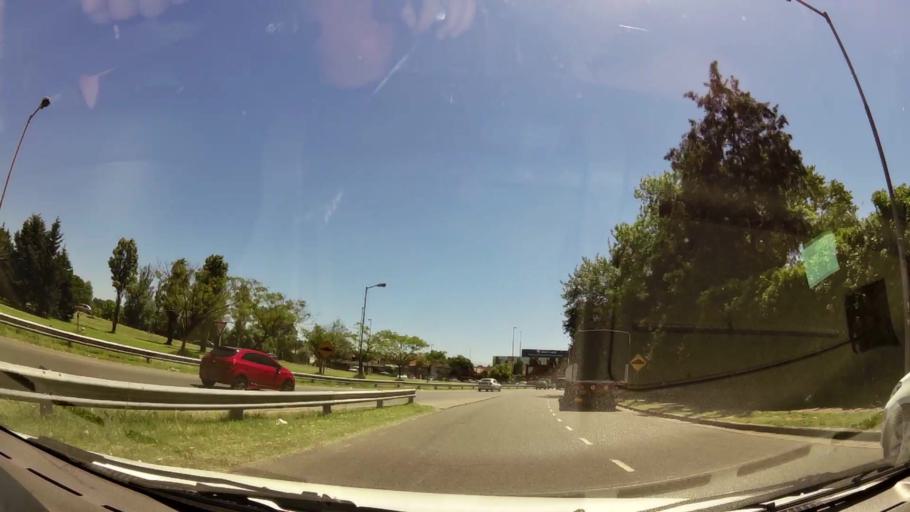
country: AR
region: Buenos Aires
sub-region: Partido de Vicente Lopez
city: Olivos
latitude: -34.5128
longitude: -58.5199
